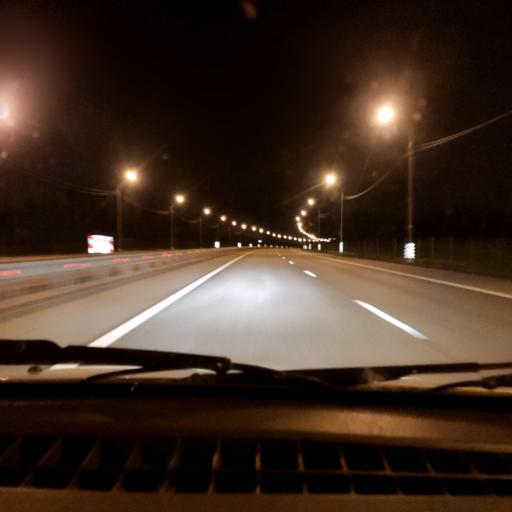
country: RU
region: Lipetsk
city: Zadonsk
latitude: 52.3383
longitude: 38.9710
